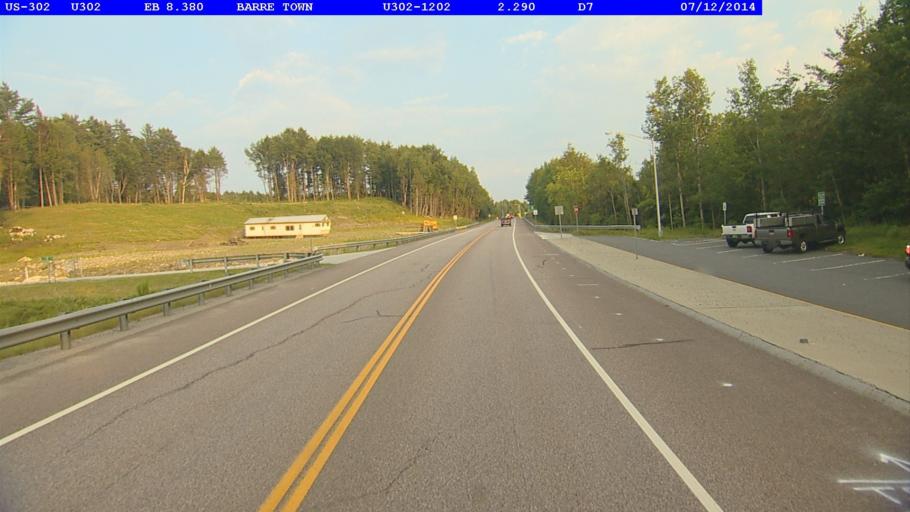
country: US
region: Vermont
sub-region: Washington County
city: South Barre
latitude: 44.1639
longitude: -72.4515
